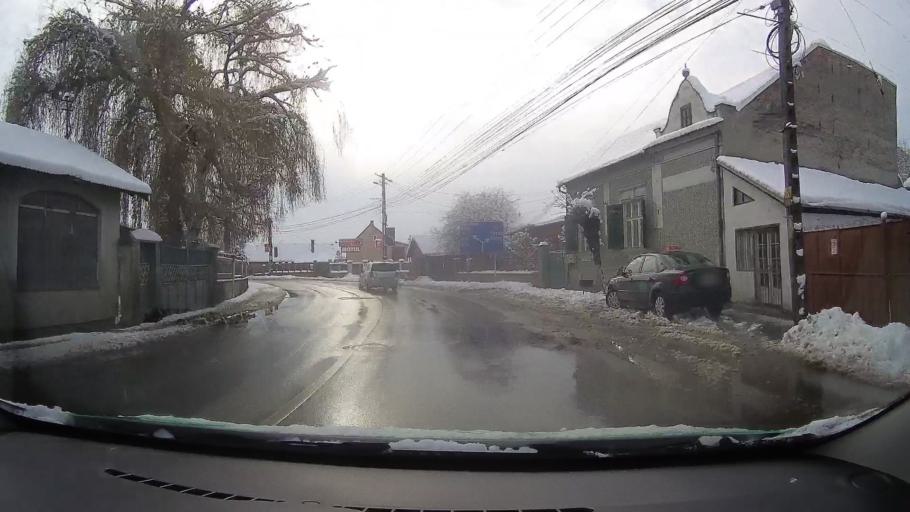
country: RO
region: Alba
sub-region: Municipiul Sebes
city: Sebes
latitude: 45.9567
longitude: 23.5651
